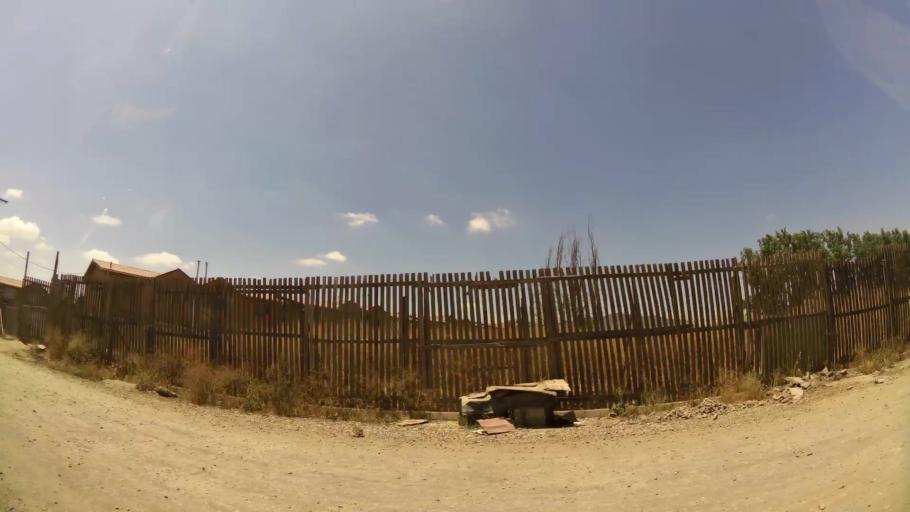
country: CL
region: Santiago Metropolitan
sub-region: Provincia de Talagante
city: Penaflor
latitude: -33.5755
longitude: -70.8004
